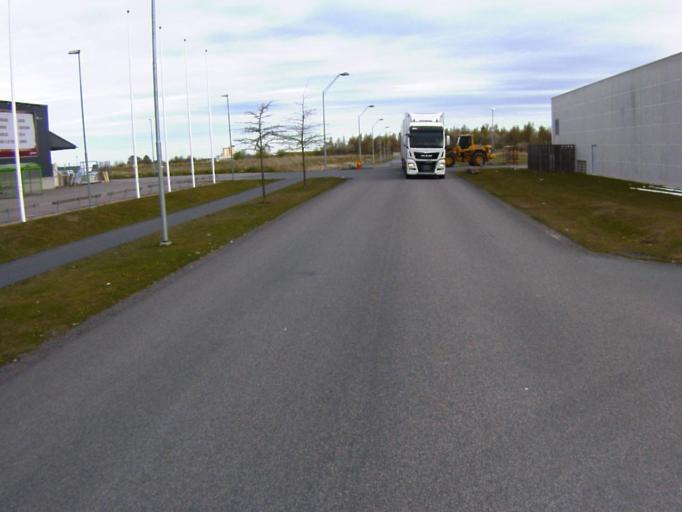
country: SE
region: Skane
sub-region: Kristianstads Kommun
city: Kristianstad
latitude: 56.0238
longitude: 14.1166
